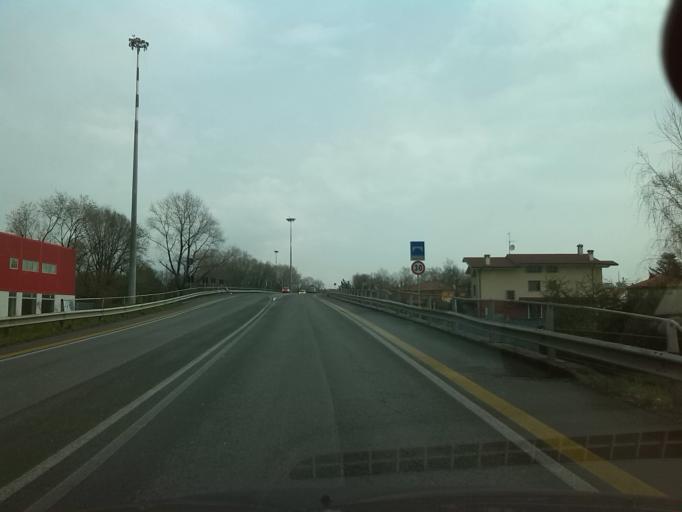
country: IT
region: Friuli Venezia Giulia
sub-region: Provincia di Gorizia
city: Savogna d'Isonzo
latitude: 45.9363
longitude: 13.5910
